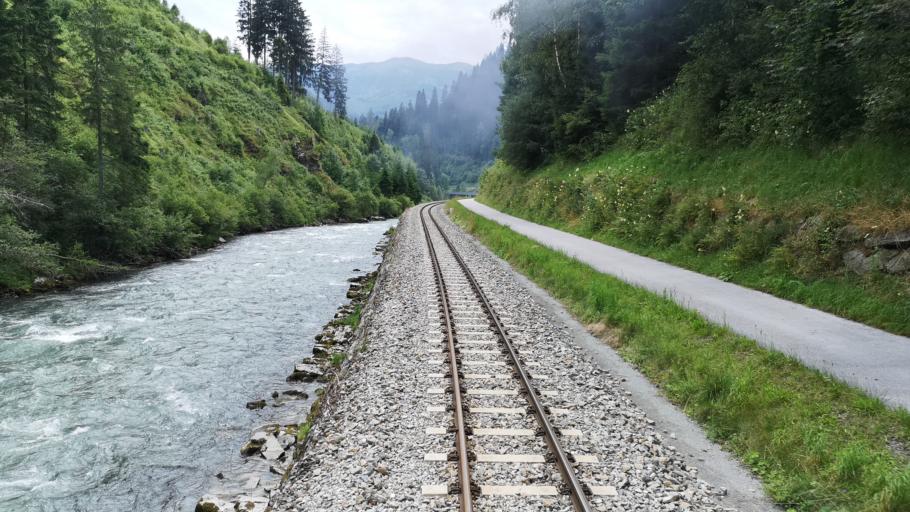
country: AT
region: Salzburg
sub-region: Politischer Bezirk Tamsweg
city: Ramingstein
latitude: 47.0861
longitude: 13.8157
